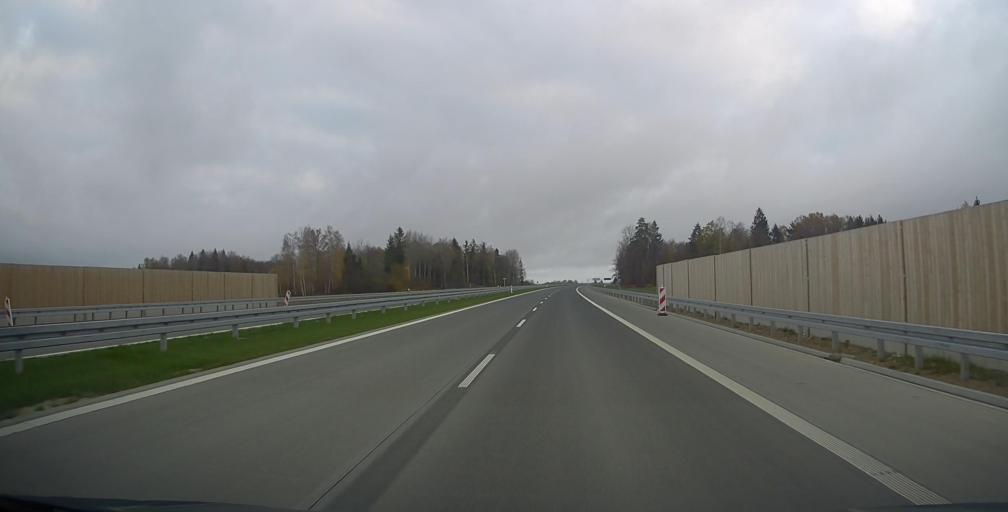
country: PL
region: Podlasie
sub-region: Powiat suwalski
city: Raczki
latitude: 53.9517
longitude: 22.7676
